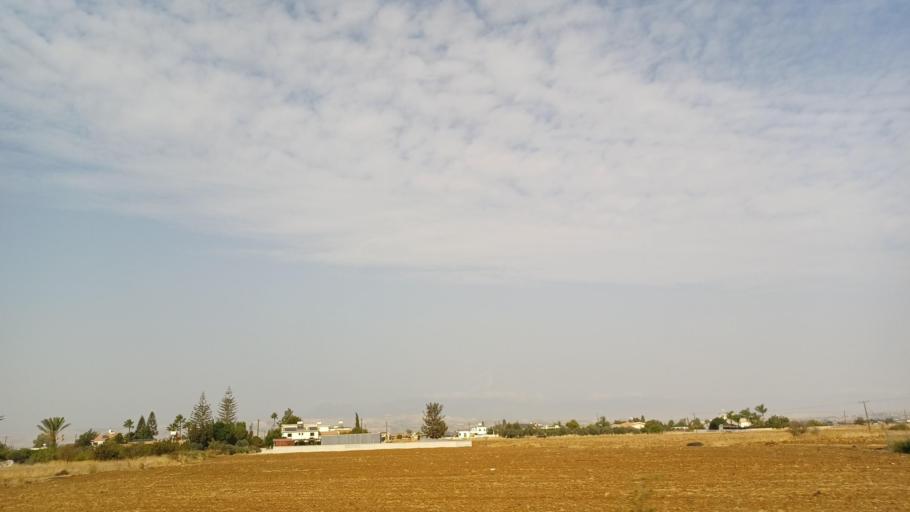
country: CY
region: Lefkosia
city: Peristerona
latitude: 35.1263
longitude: 33.0888
